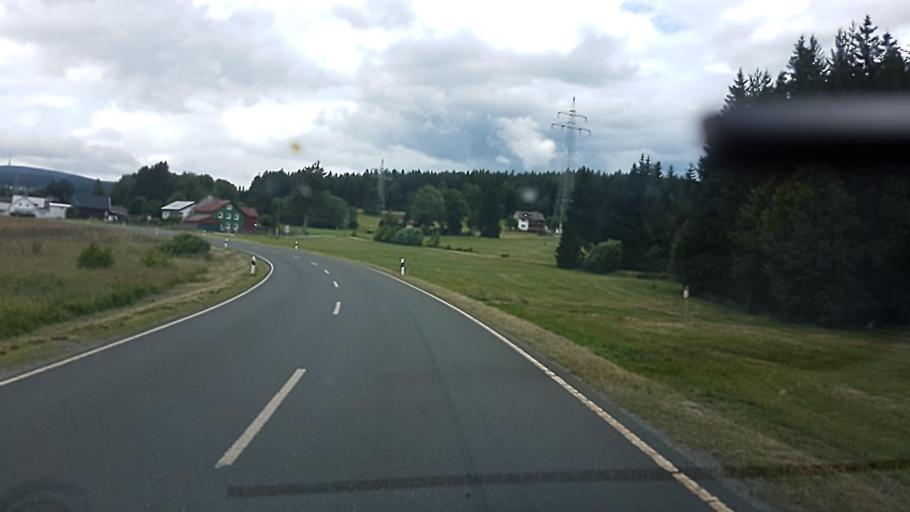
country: DE
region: Bavaria
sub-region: Upper Franconia
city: Mehlmeisel
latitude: 49.9800
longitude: 11.8684
